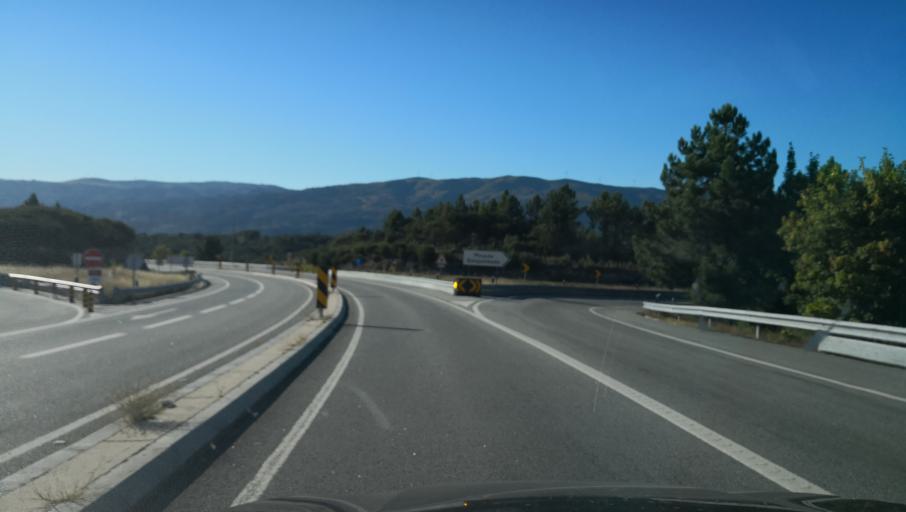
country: PT
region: Vila Real
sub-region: Vila Real
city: Vila Real
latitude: 41.3288
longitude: -7.6738
